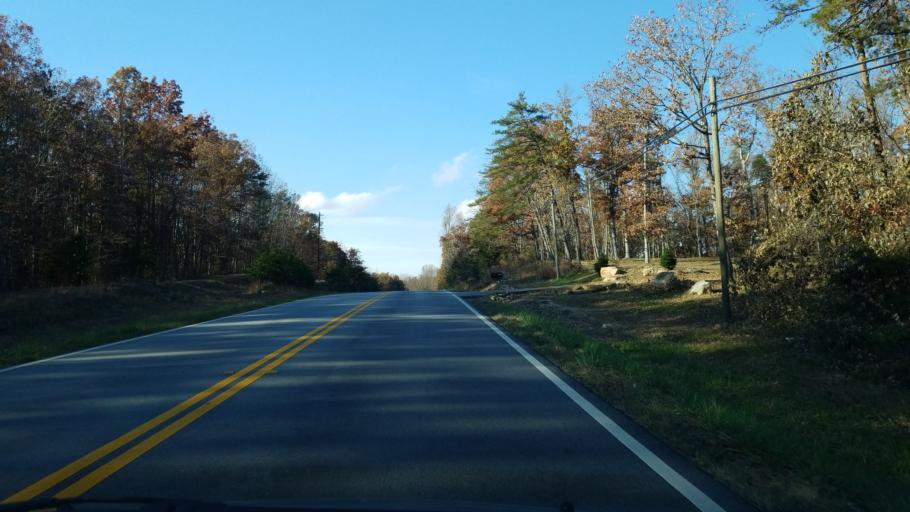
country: US
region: Georgia
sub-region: Dade County
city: Trenton
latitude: 34.8209
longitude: -85.4982
